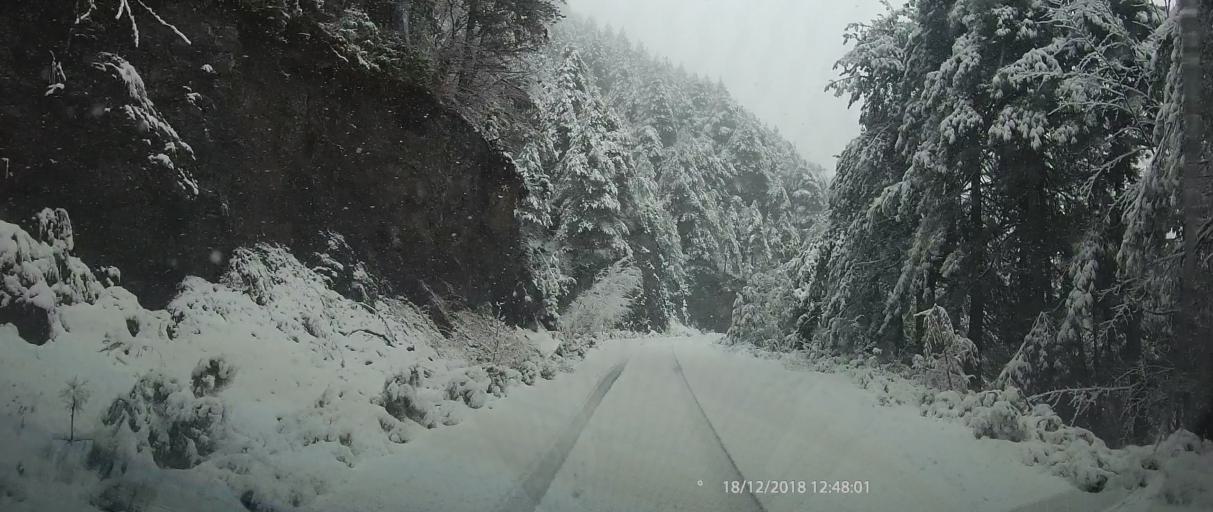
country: GR
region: Central Macedonia
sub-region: Nomos Pierias
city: Litochoro
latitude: 40.1016
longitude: 22.4376
